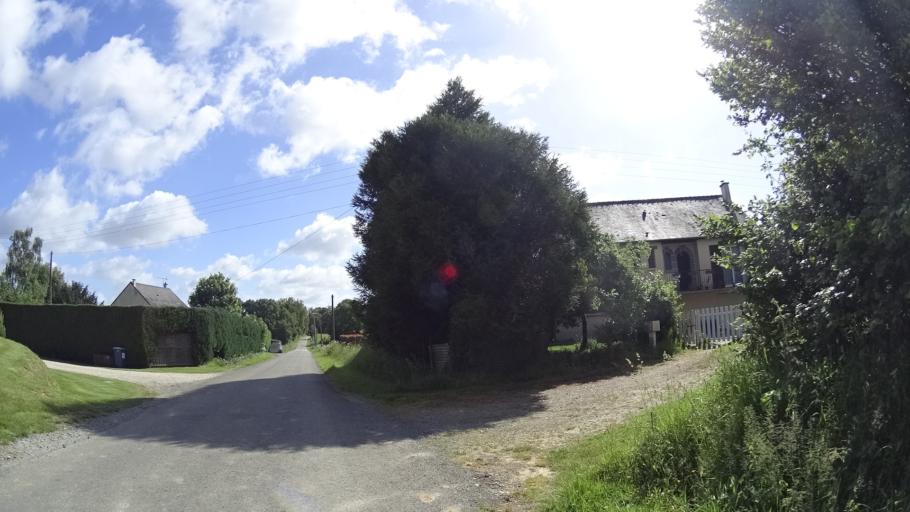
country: FR
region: Brittany
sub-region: Departement d'Ille-et-Vilaine
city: Melesse
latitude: 48.2058
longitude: -1.7179
